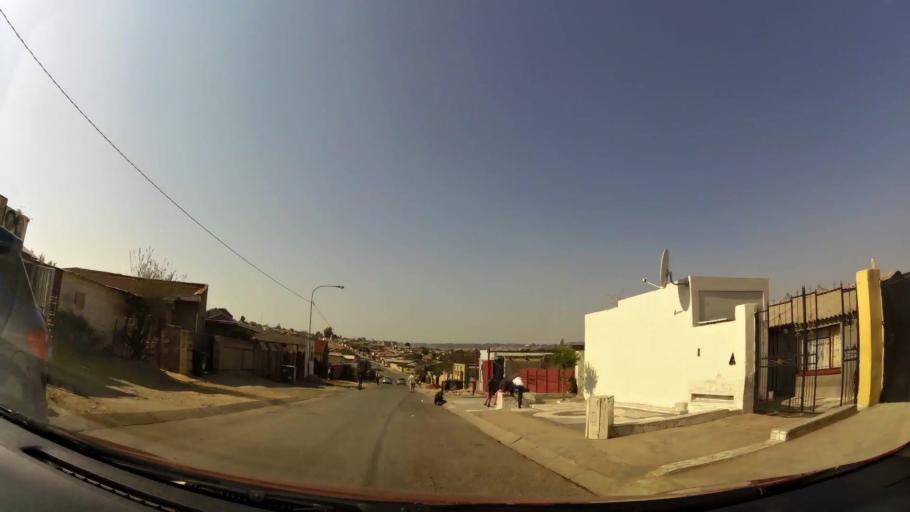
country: ZA
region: Gauteng
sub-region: City of Johannesburg Metropolitan Municipality
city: Soweto
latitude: -26.2493
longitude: 27.9351
